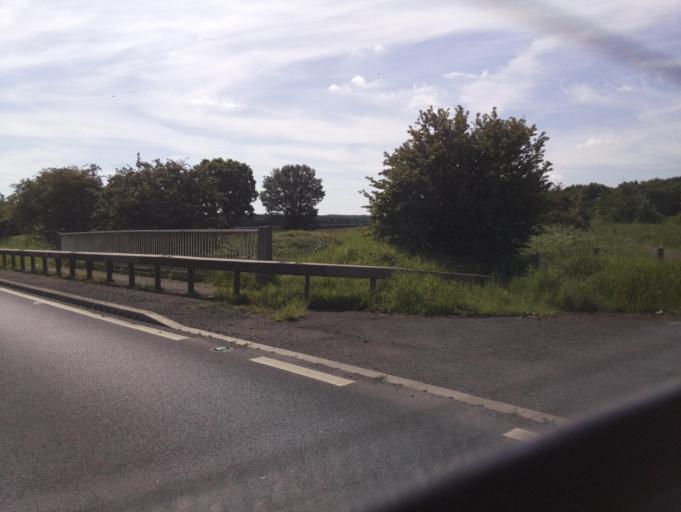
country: GB
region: England
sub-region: North Lincolnshire
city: Bottesford
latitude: 53.5636
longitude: -0.6051
